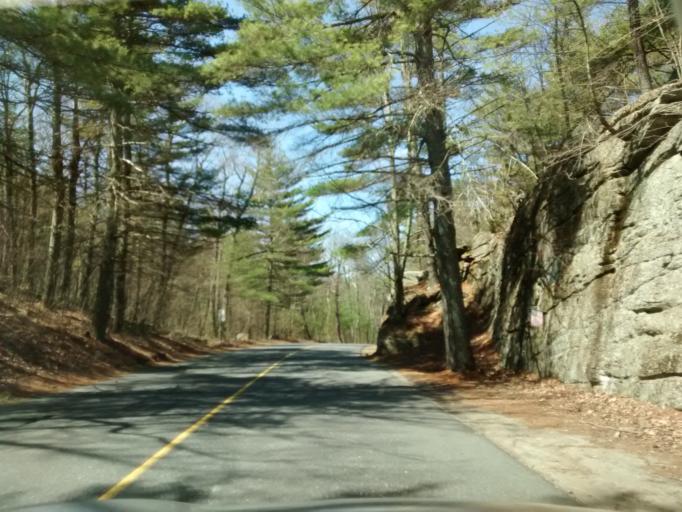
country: US
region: Massachusetts
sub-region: Worcester County
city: Sutton
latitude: 42.1325
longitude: -71.7184
